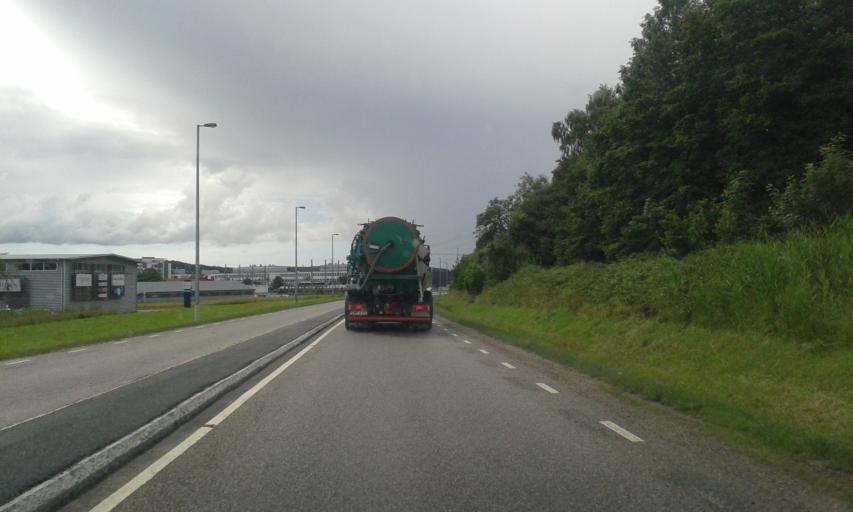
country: SE
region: Vaestra Goetaland
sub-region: Kungalvs Kommun
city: Kungalv
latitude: 57.8811
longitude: 11.9801
